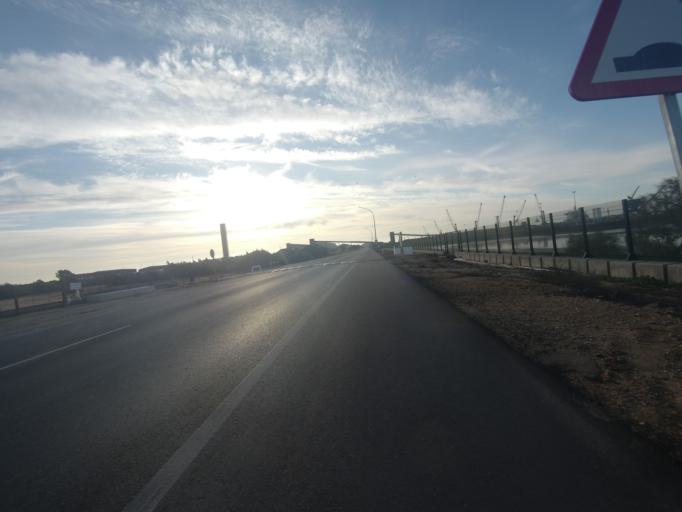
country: ES
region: Andalusia
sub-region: Provincia de Huelva
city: Punta Umbria
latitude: 37.2012
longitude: -6.9362
